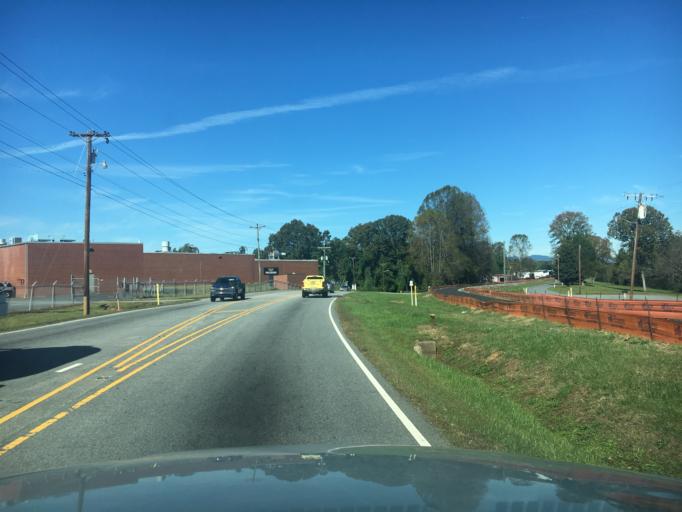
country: US
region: North Carolina
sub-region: Rutherford County
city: Rutherfordton
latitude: 35.3772
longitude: -81.9454
